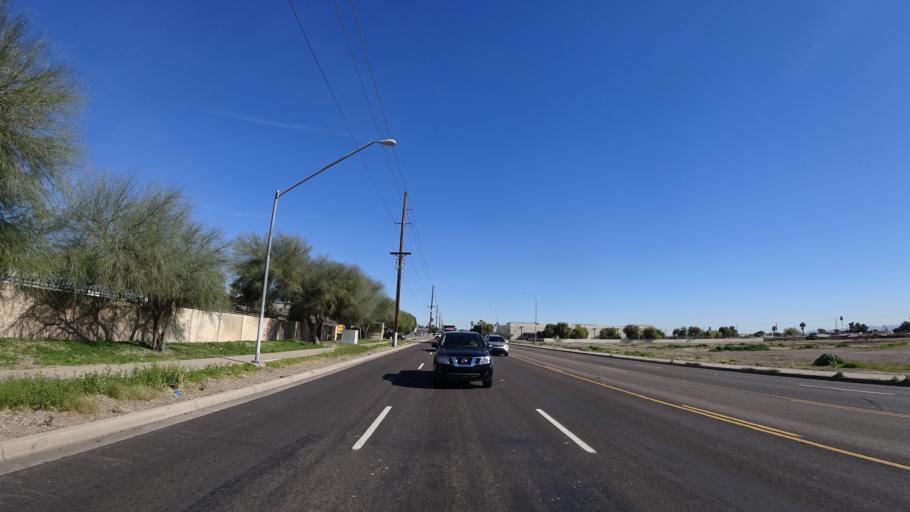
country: US
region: Arizona
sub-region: Maricopa County
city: Glendale
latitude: 33.5095
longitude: -112.1636
